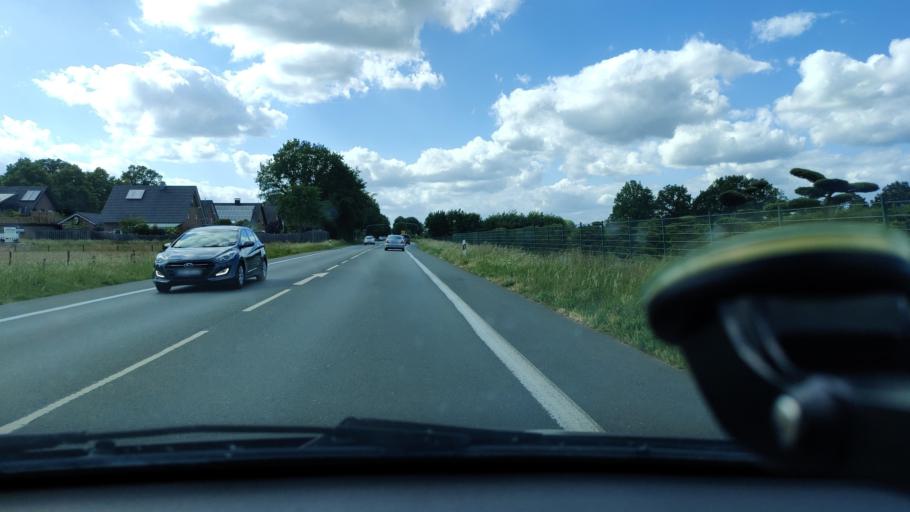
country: DE
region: North Rhine-Westphalia
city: Stadtlohn
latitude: 51.9823
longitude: 6.9511
